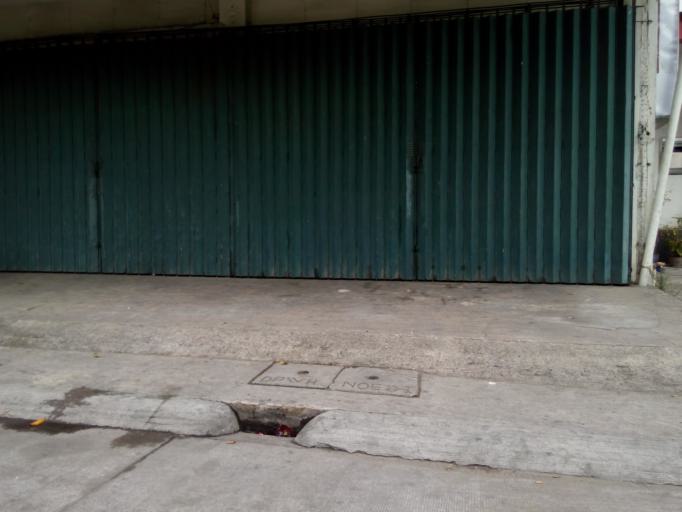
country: PH
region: Central Visayas
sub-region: Province of Negros Oriental
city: Dumaguete
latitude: 9.3074
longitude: 123.3056
